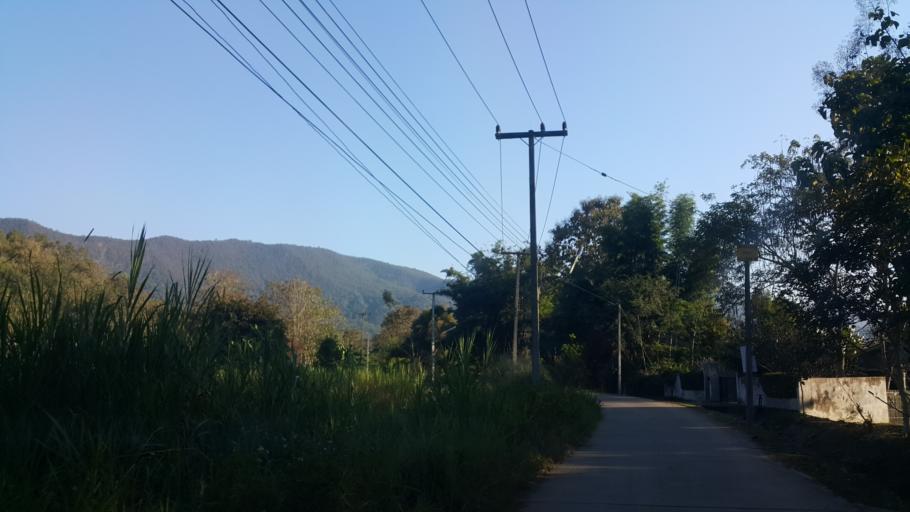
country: TH
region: Chiang Mai
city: Mae On
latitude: 18.7708
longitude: 99.2643
